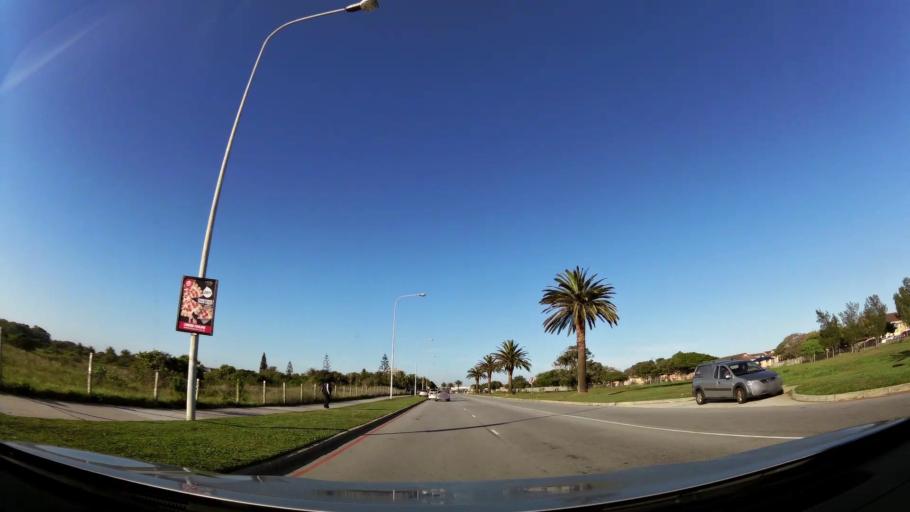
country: ZA
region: Eastern Cape
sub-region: Nelson Mandela Bay Metropolitan Municipality
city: Port Elizabeth
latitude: -33.9965
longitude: 25.6705
